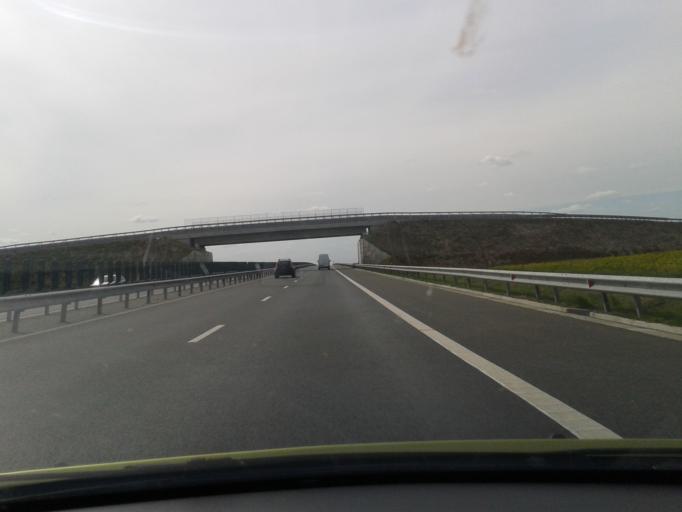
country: RO
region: Timis
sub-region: Oras Recas
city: Recas
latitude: 45.8136
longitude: 21.4984
